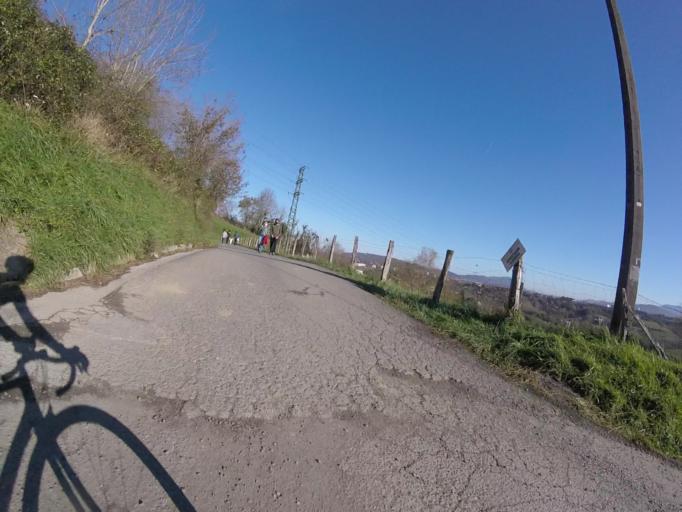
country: ES
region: Basque Country
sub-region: Provincia de Guipuzcoa
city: Lasarte
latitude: 43.2893
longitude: -2.0056
